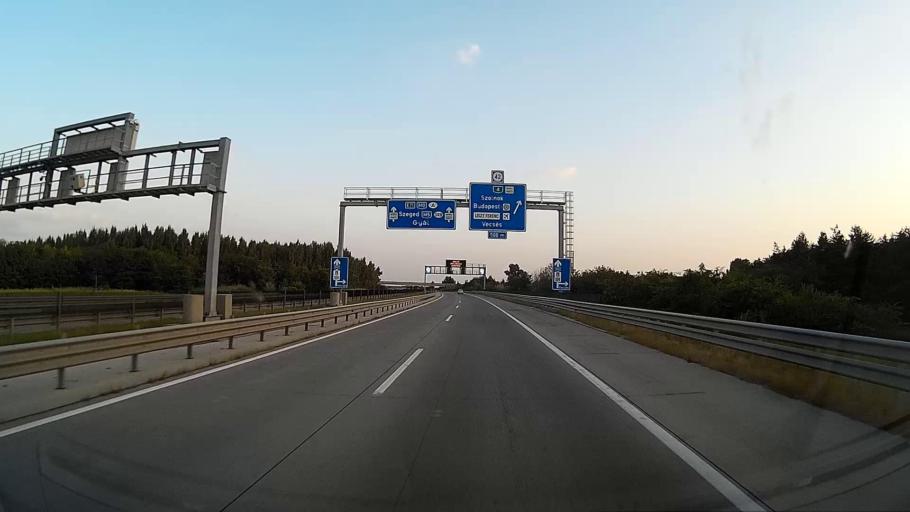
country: HU
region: Pest
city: Ecser
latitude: 47.4174
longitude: 19.3157
